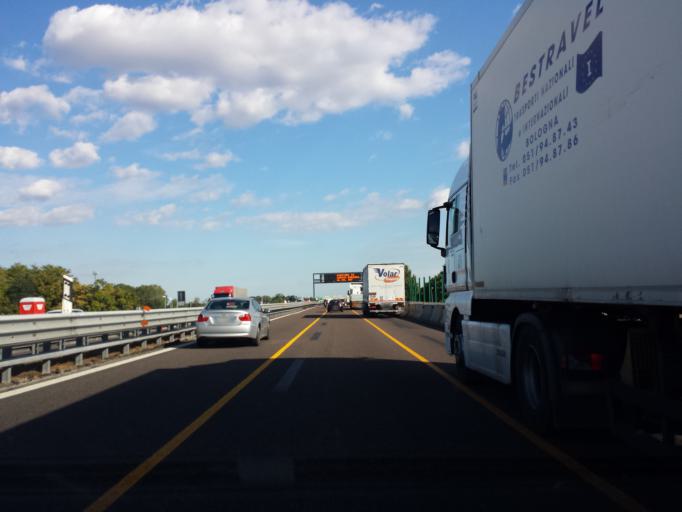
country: IT
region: Veneto
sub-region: Provincia di Padova
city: Villaguattera
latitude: 45.4508
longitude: 11.8294
